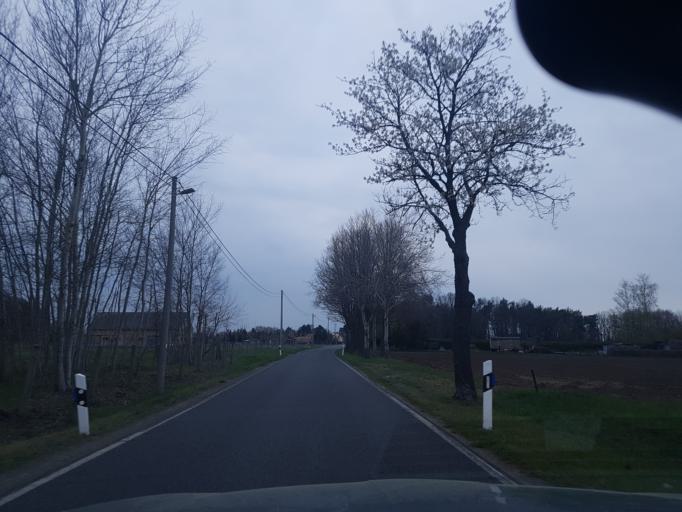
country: DE
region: Brandenburg
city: Falkenberg
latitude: 51.5907
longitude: 13.3129
